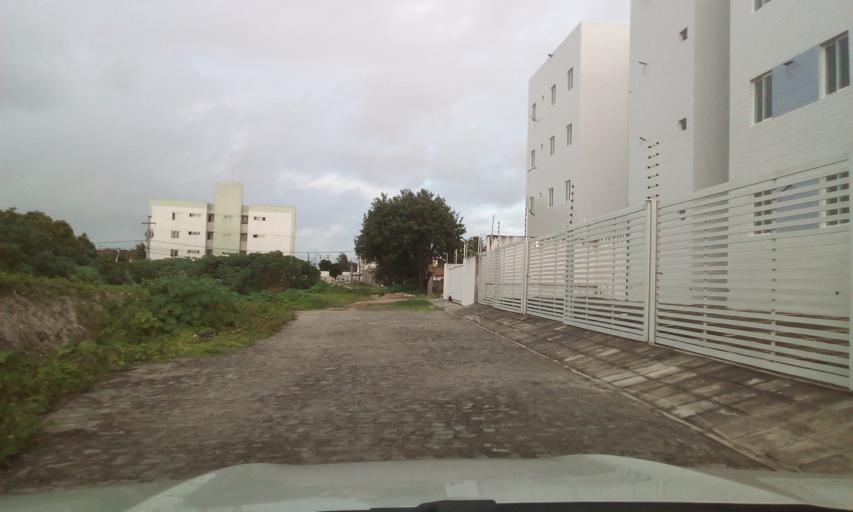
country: BR
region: Paraiba
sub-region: Joao Pessoa
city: Joao Pessoa
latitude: -7.1638
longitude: -34.8549
